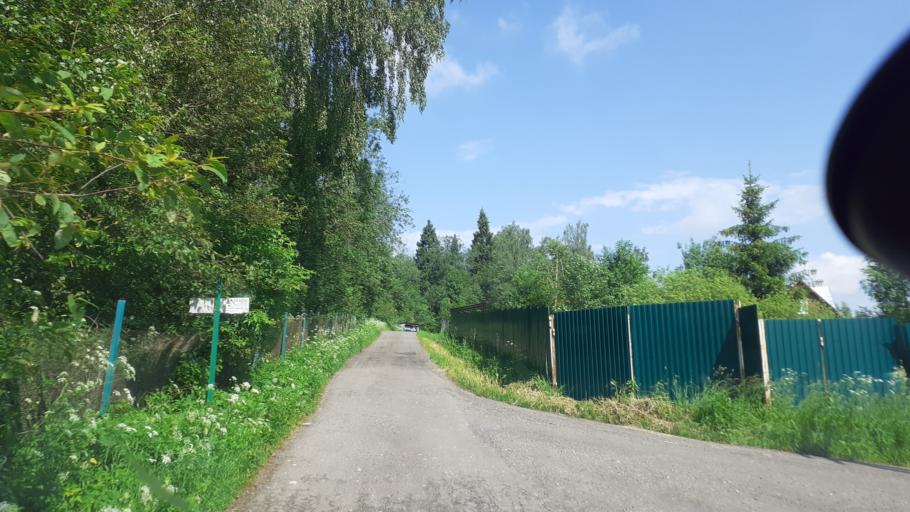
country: RU
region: Moskovskaya
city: Ateptsevo
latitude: 55.3034
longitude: 36.7647
